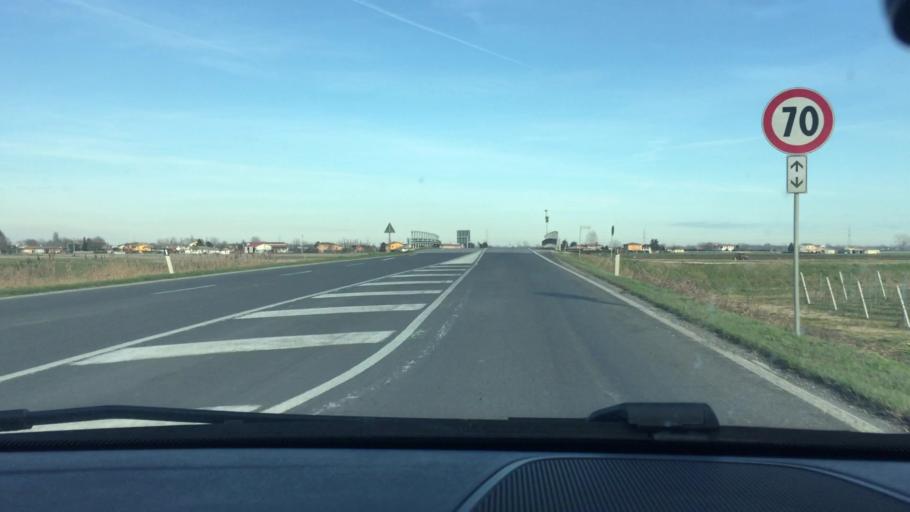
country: IT
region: Veneto
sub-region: Provincia di Padova
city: Correzzola
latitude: 45.2161
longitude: 12.1059
